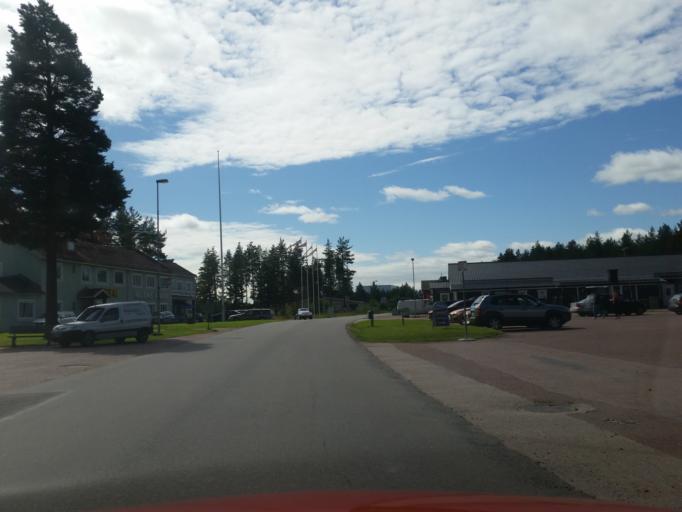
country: SE
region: Dalarna
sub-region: Leksand Municipality
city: Smedby
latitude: 60.6705
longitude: 15.0908
